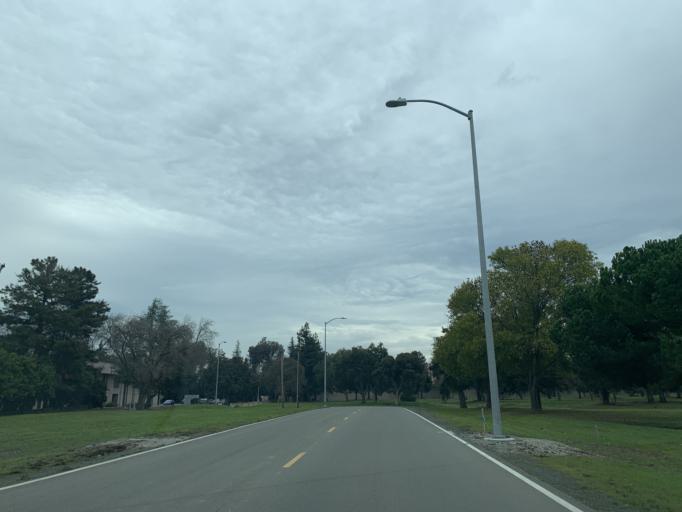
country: US
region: California
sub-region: Santa Clara County
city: Mountain View
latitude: 37.4110
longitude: -122.0669
